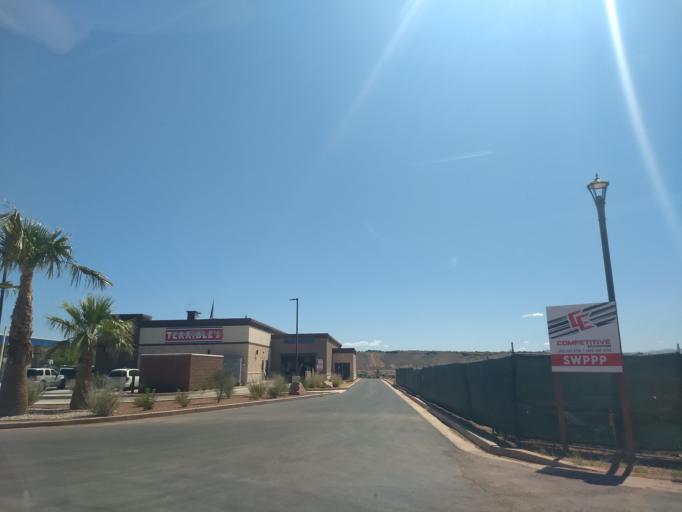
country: US
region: Utah
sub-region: Washington County
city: Washington
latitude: 37.1434
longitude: -113.4873
